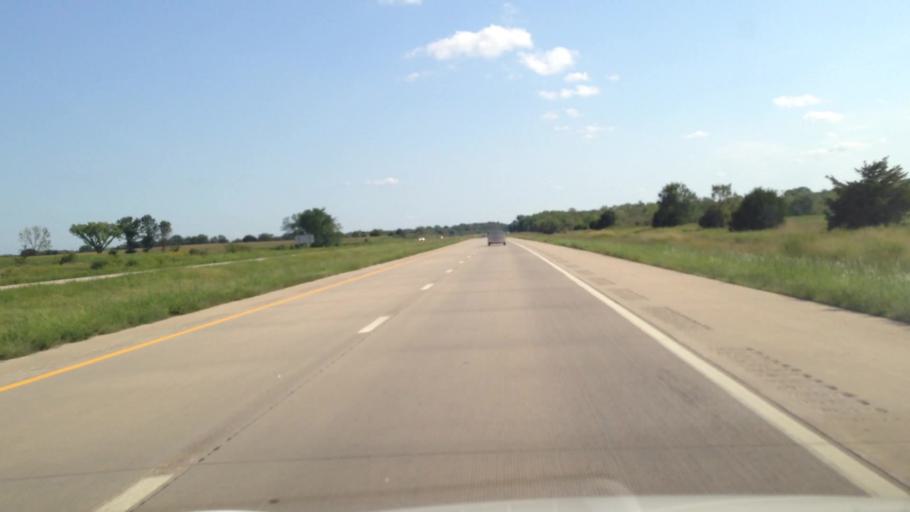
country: US
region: Kansas
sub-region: Bourbon County
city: Fort Scott
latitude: 37.9180
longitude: -94.7045
